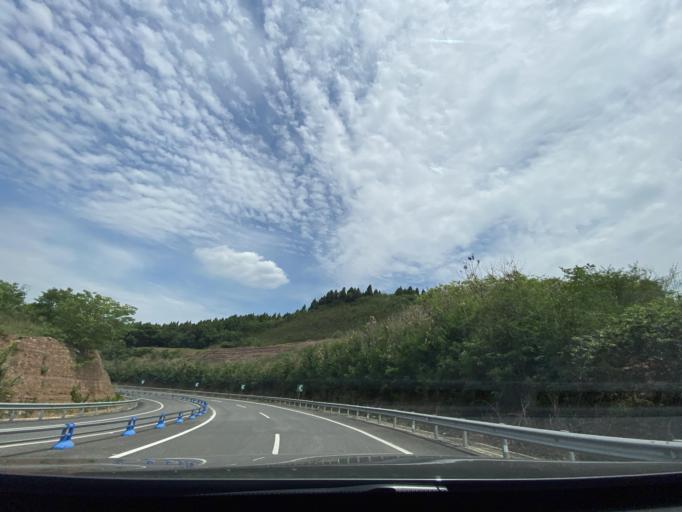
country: CN
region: Sichuan
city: Mianyang
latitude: 31.3495
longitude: 104.7066
